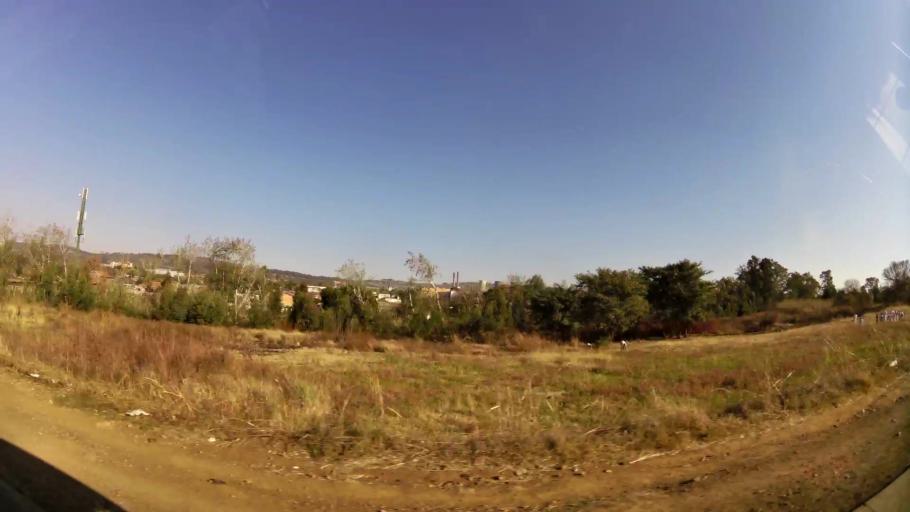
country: ZA
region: Gauteng
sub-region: City of Tshwane Metropolitan Municipality
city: Pretoria
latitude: -25.7437
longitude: 28.1500
